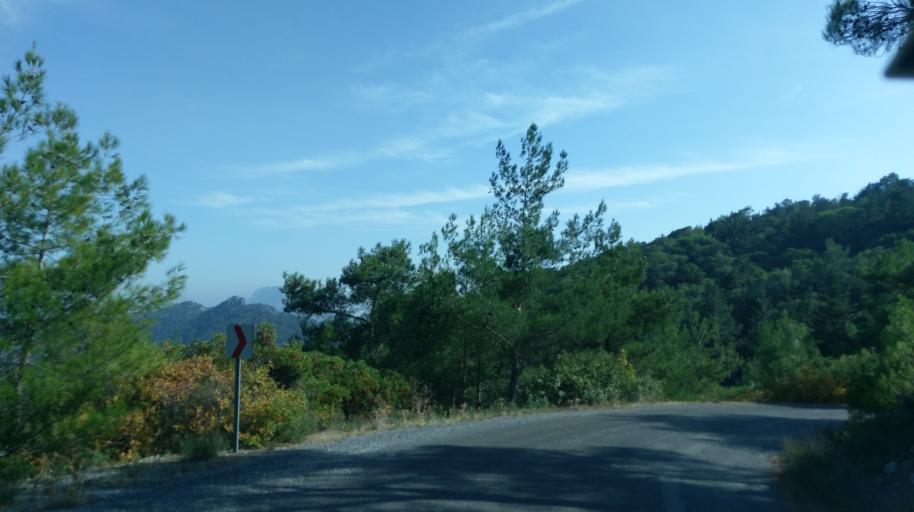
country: CY
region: Keryneia
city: Kyrenia
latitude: 35.3065
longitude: 33.2569
